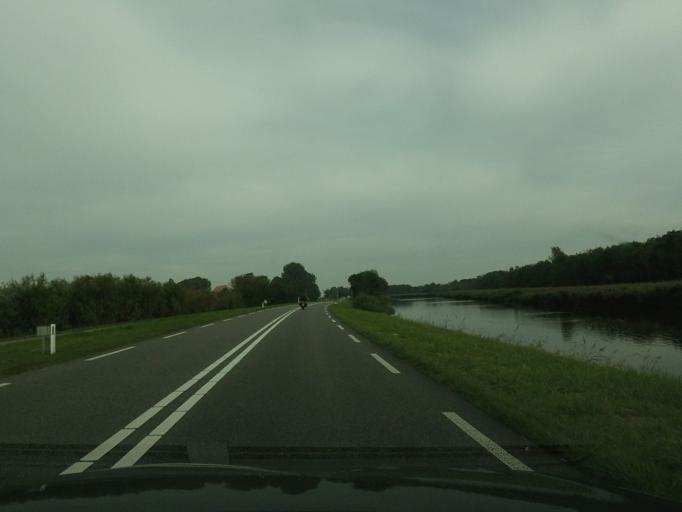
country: NL
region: North Holland
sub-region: Gemeente Schagen
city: Schagen
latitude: 52.8664
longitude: 4.8449
